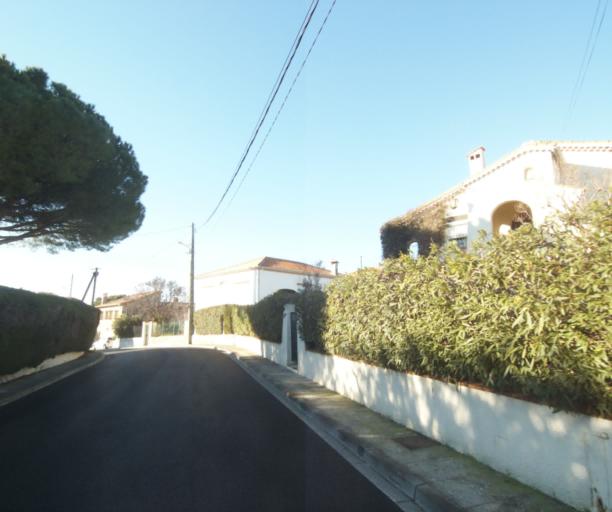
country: FR
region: Provence-Alpes-Cote d'Azur
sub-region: Departement des Alpes-Maritimes
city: Antibes
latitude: 43.5816
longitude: 7.1030
